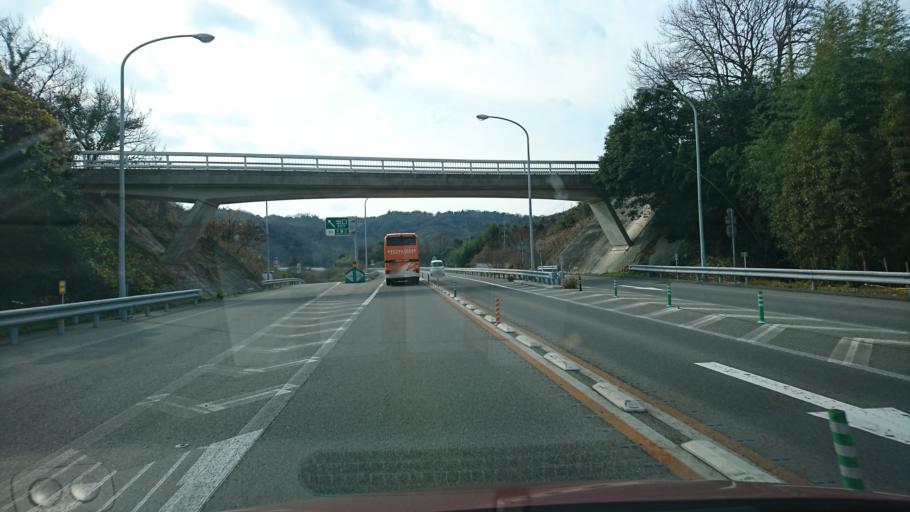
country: JP
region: Hiroshima
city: Innoshima
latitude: 34.1713
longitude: 133.0660
